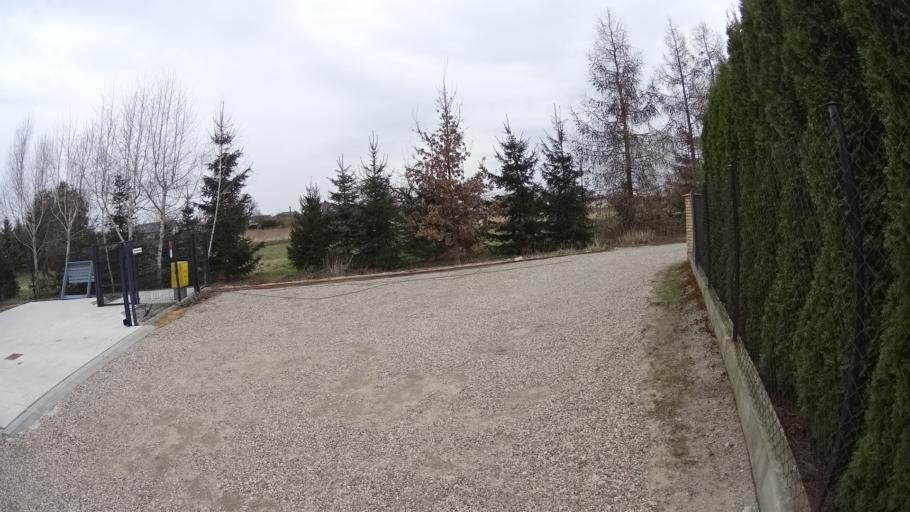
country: PL
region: Masovian Voivodeship
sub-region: Powiat warszawski zachodni
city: Stare Babice
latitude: 52.2474
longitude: 20.8237
